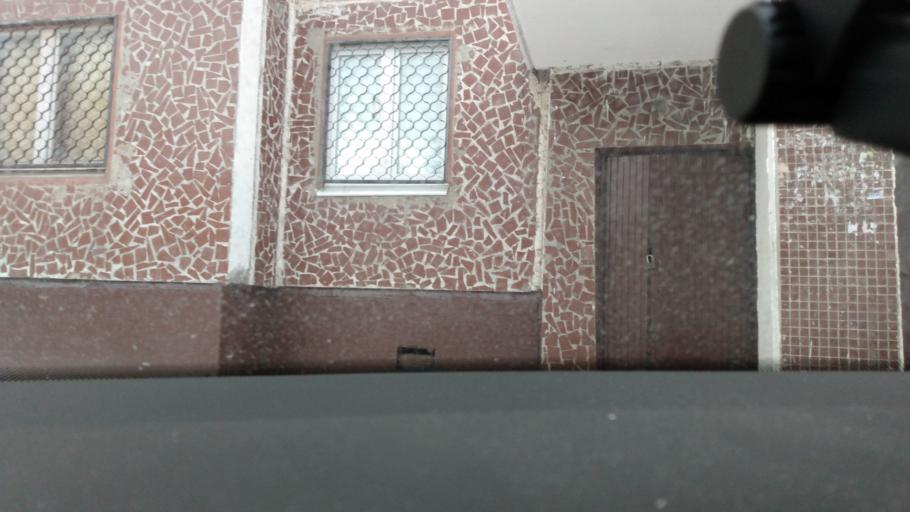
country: RU
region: Moskovskaya
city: Shchelkovo
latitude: 55.9179
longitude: 37.9873
